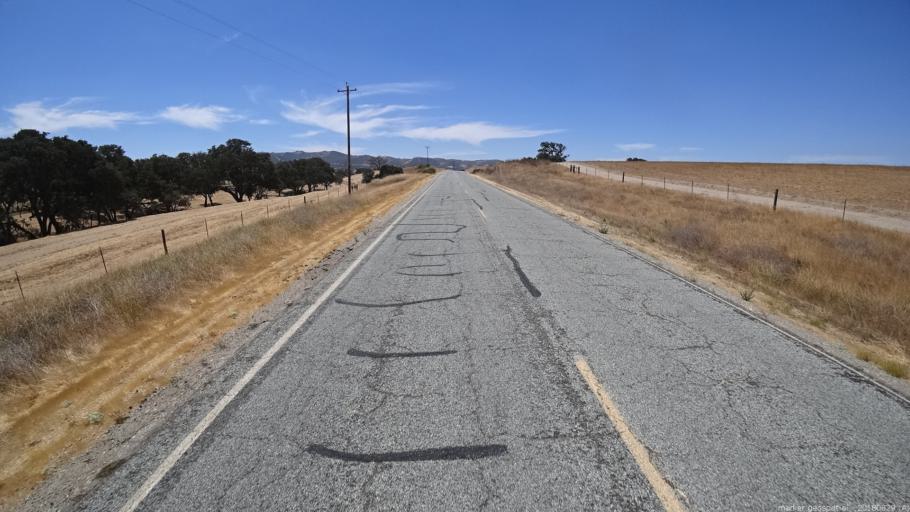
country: US
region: California
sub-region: San Luis Obispo County
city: Lake Nacimiento
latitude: 35.8685
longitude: -120.8492
